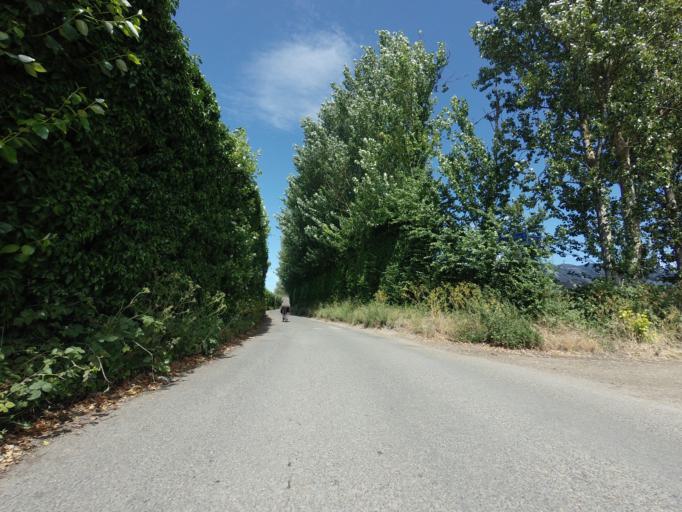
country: GB
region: England
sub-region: Kent
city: Strood
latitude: 51.4197
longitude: 0.4963
